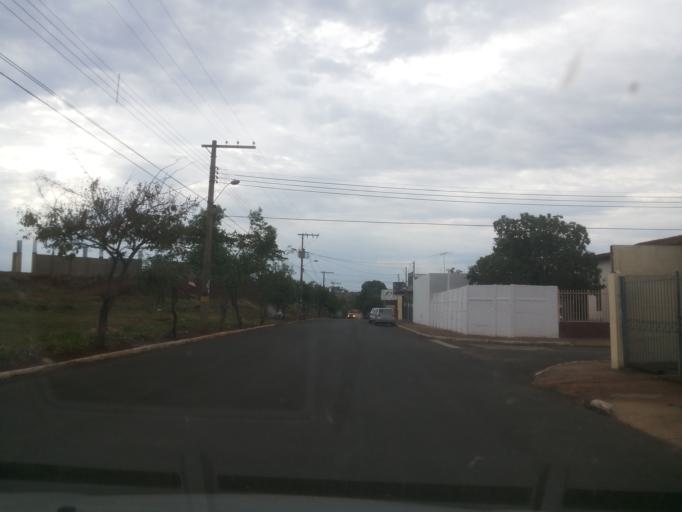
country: BR
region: Minas Gerais
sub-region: Ituiutaba
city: Ituiutaba
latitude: -18.9737
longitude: -49.4769
